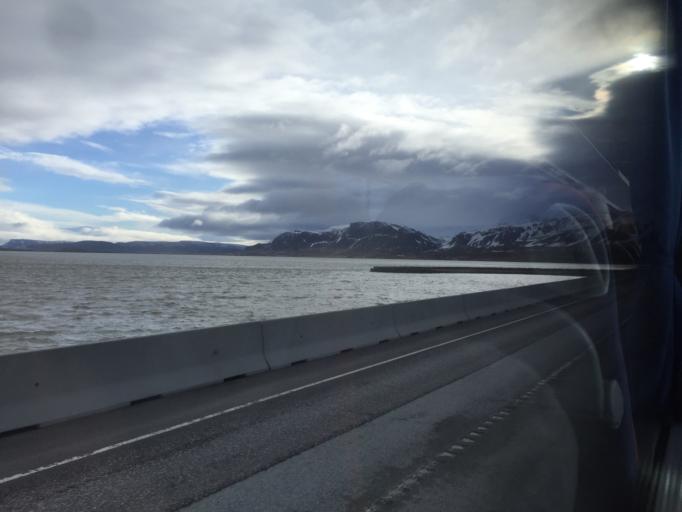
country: IS
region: West
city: Borgarnes
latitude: 64.5370
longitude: -21.9016
